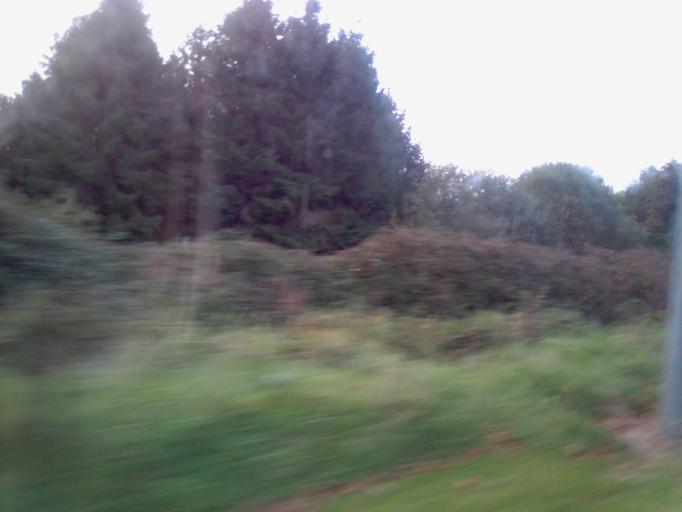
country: IE
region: Munster
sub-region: An Clar
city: Shannon
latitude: 52.7117
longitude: -8.8828
